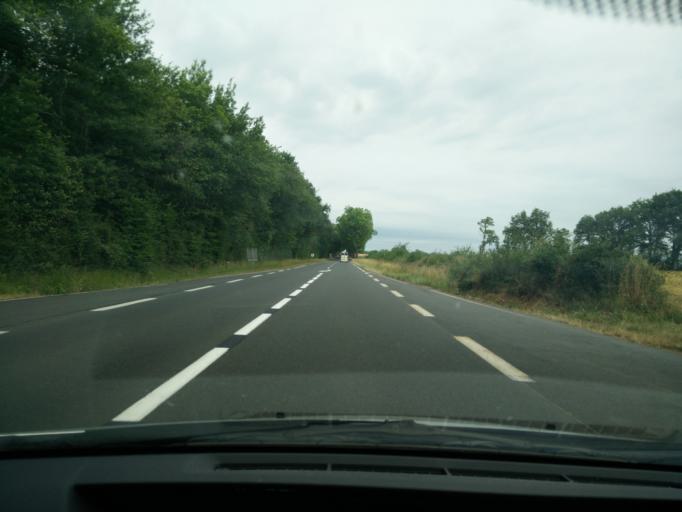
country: FR
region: Pays de la Loire
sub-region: Departement de Maine-et-Loire
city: Saint-Jean
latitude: 47.3082
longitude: -0.3965
